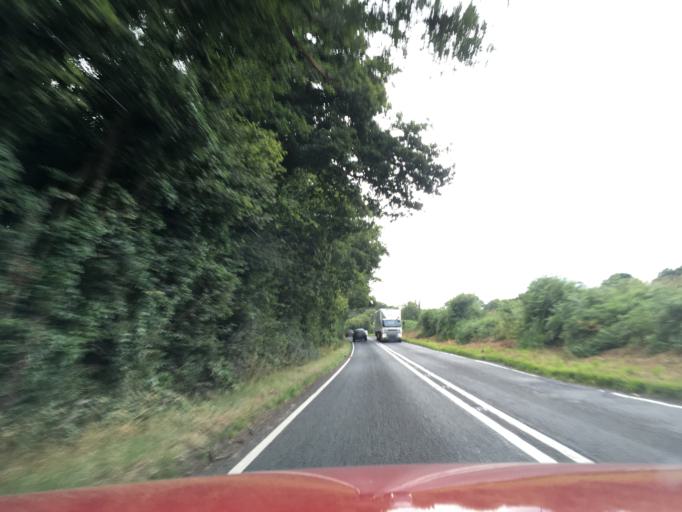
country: GB
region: England
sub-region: Hampshire
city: Four Marks
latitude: 51.0310
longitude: -1.0818
